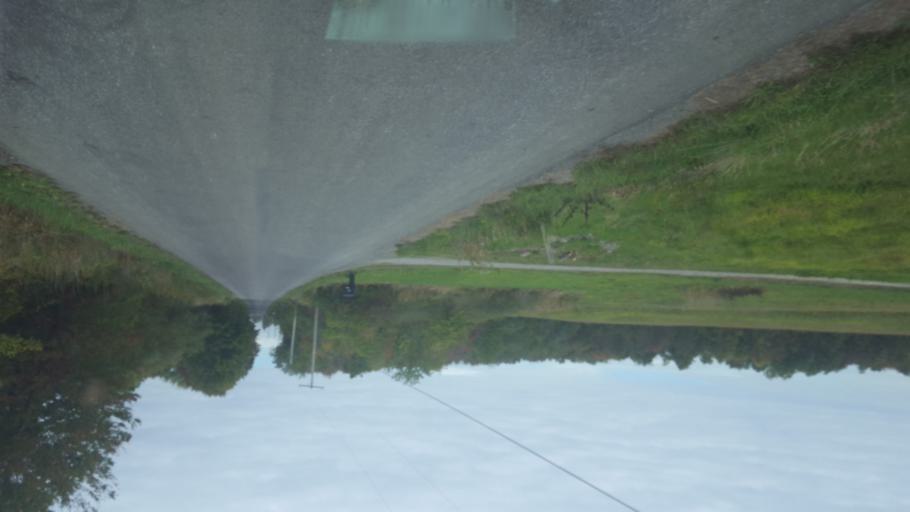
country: US
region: Pennsylvania
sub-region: Mercer County
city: Stoneboro
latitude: 41.3741
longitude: -80.2435
